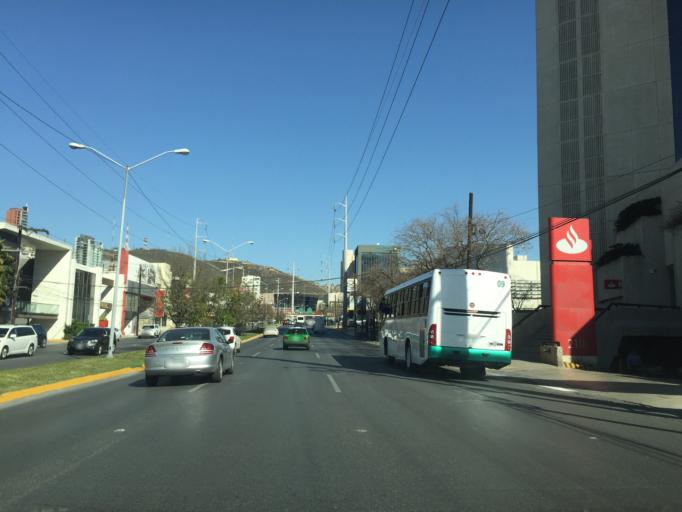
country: MX
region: Nuevo Leon
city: Garza Garcia
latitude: 25.6534
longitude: -100.3442
